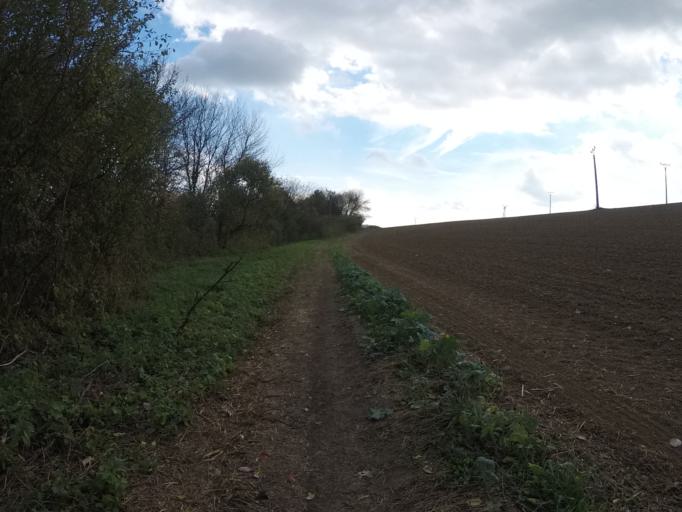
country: SK
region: Presovsky
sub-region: Okres Presov
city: Presov
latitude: 48.9310
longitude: 21.1815
